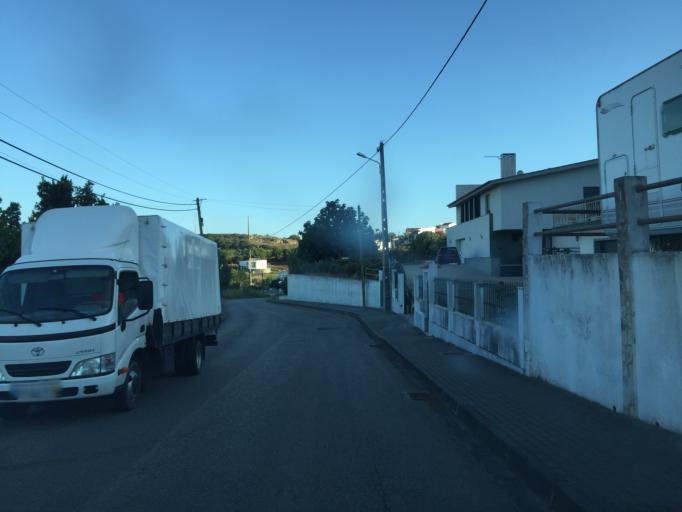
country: PT
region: Lisbon
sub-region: Torres Vedras
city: Torres Vedras
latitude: 39.0897
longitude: -9.2731
